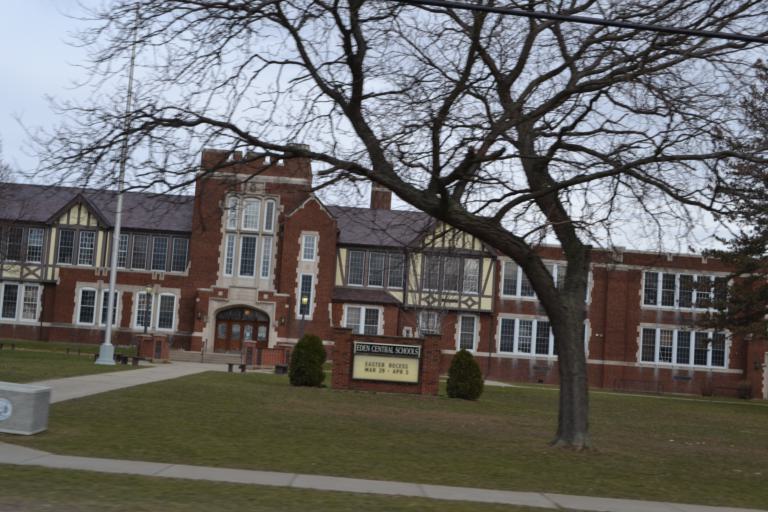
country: US
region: New York
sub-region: Erie County
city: Eden
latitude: 42.6614
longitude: -78.8921
